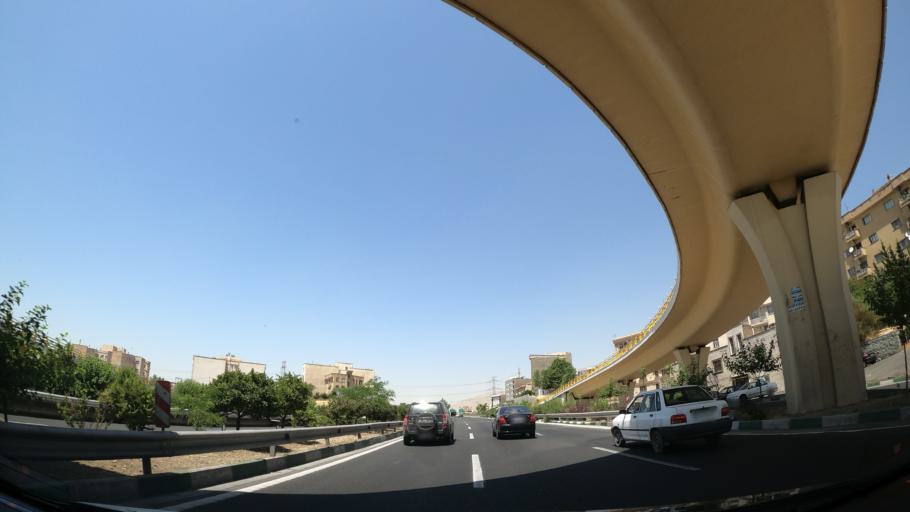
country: IR
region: Tehran
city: Tajrish
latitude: 35.7704
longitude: 51.3231
